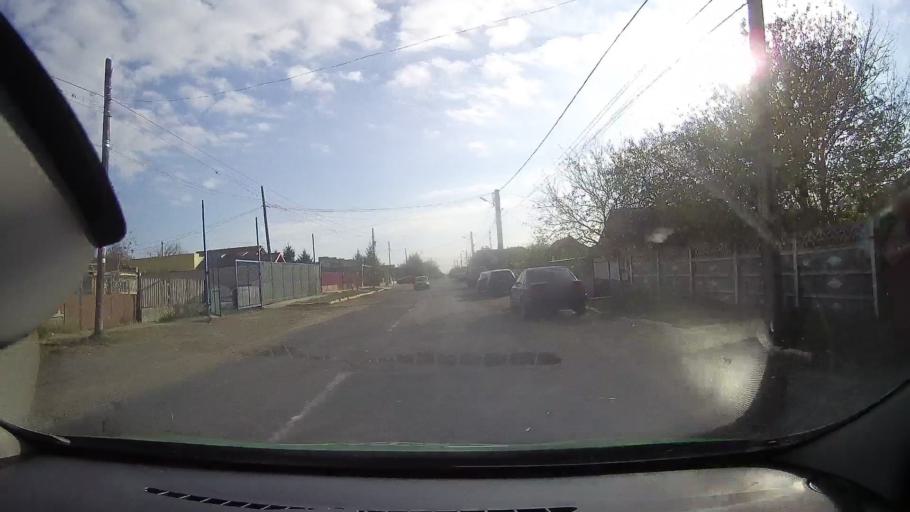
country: RO
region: Constanta
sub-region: Comuna Corbu
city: Corbu
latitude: 44.3989
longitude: 28.6617
